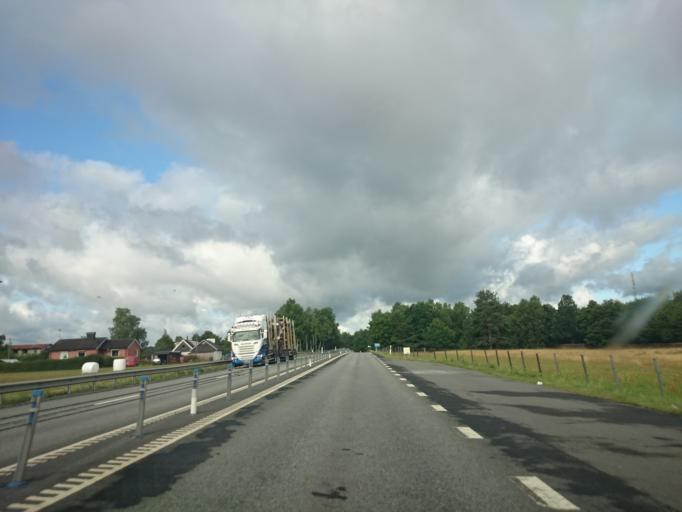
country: SE
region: Skane
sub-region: Kristianstads Kommun
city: Onnestad
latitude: 55.9329
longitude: 14.0019
